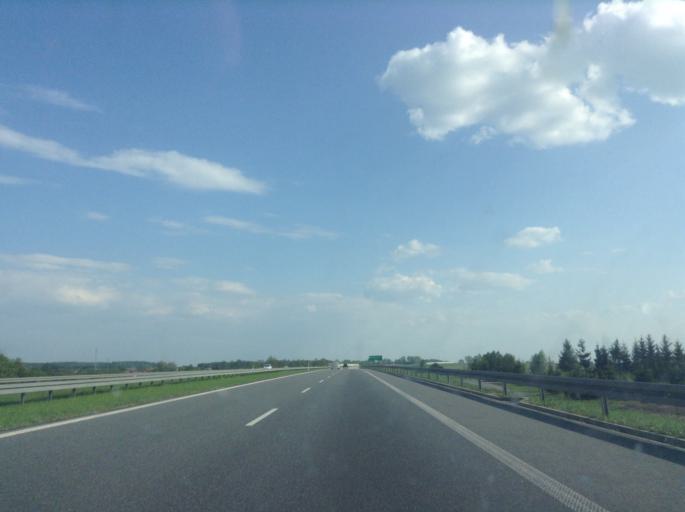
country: PL
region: Warmian-Masurian Voivodeship
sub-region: Powiat elblaski
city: Paslek
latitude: 53.9999
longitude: 19.6871
